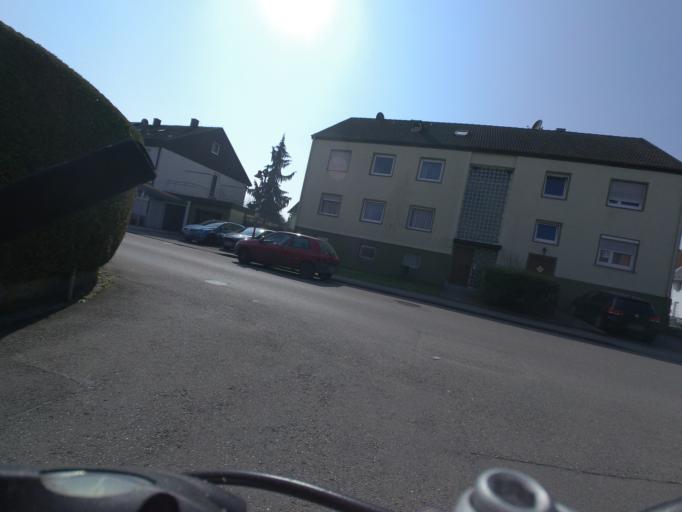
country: DE
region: Baden-Wuerttemberg
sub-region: Regierungsbezirk Stuttgart
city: Unterensingen
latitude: 48.6591
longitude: 9.3569
